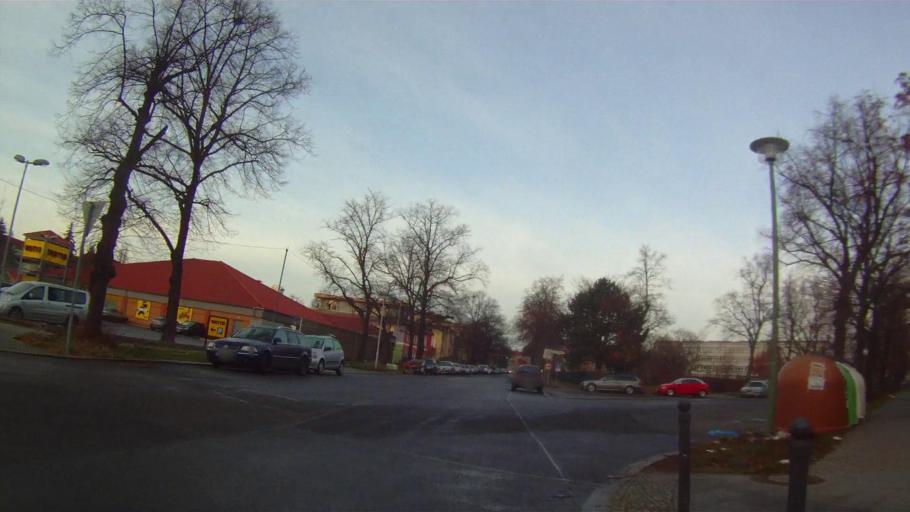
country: DE
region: Berlin
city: Johannisthal
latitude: 52.4451
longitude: 13.5115
